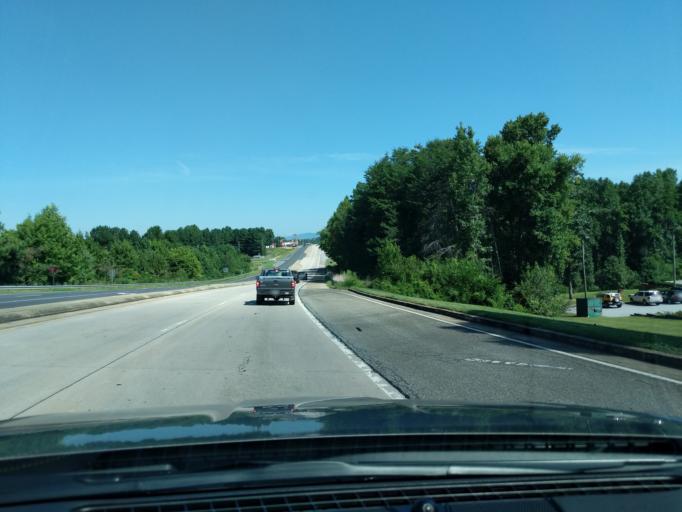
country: US
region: Georgia
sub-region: Habersham County
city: Baldwin
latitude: 34.5036
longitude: -83.5452
